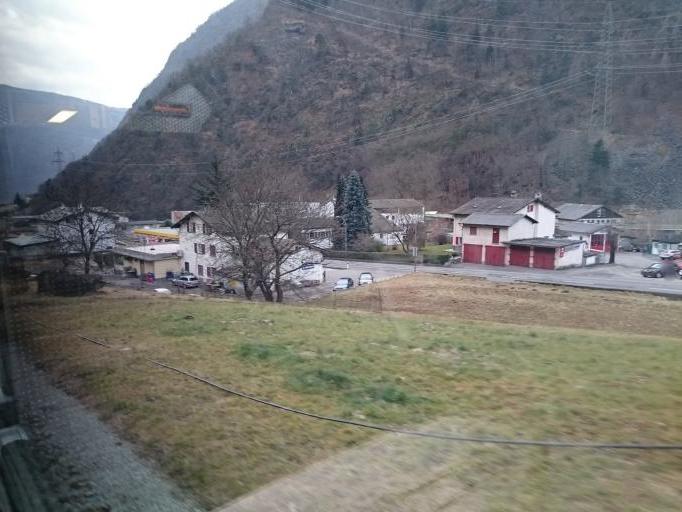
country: CH
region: Grisons
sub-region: Bernina District
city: Brusio
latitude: 46.2392
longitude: 10.1365
